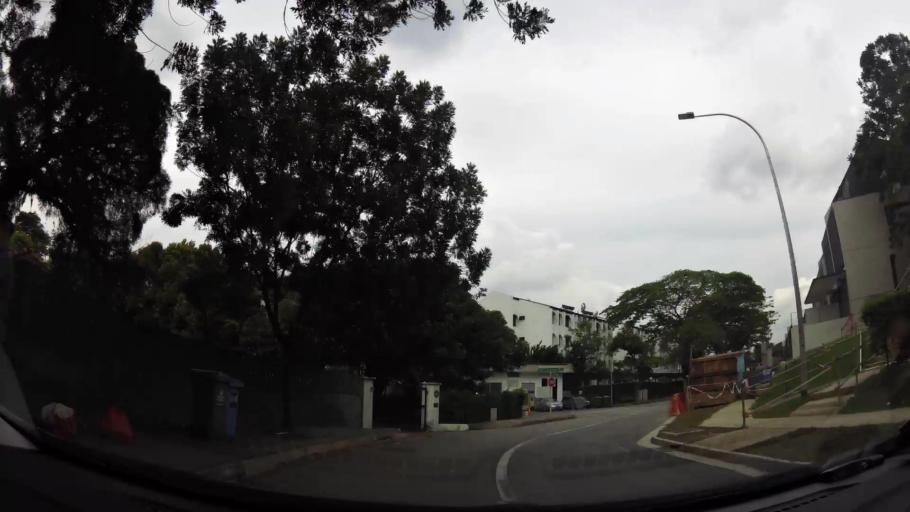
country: SG
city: Singapore
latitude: 1.3223
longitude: 103.8018
